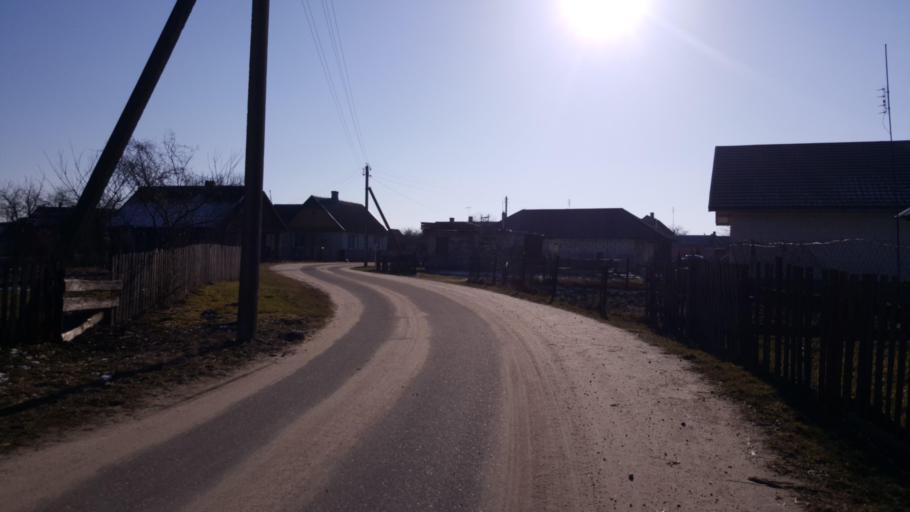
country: BY
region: Brest
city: Kamyanyets
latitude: 52.3843
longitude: 23.7959
